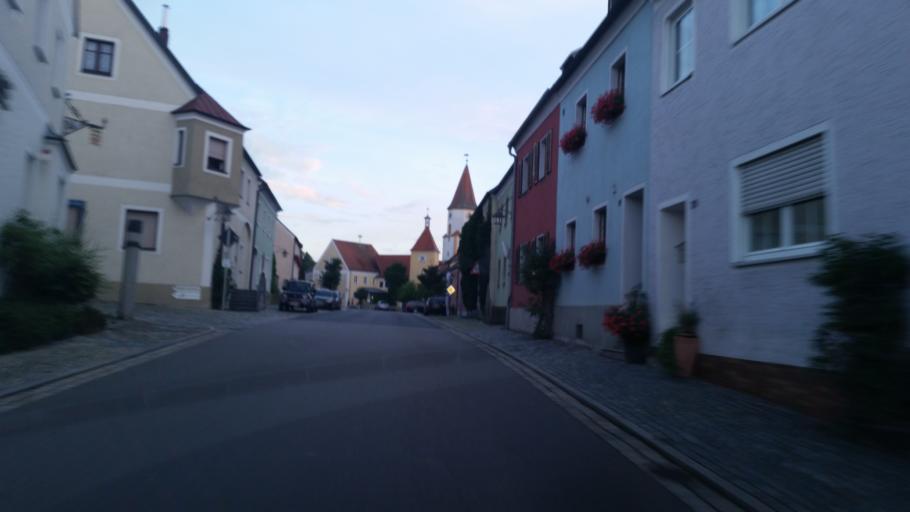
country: DE
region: Bavaria
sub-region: Upper Palatinate
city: Luhe-Wildenau
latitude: 49.5839
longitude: 12.1485
